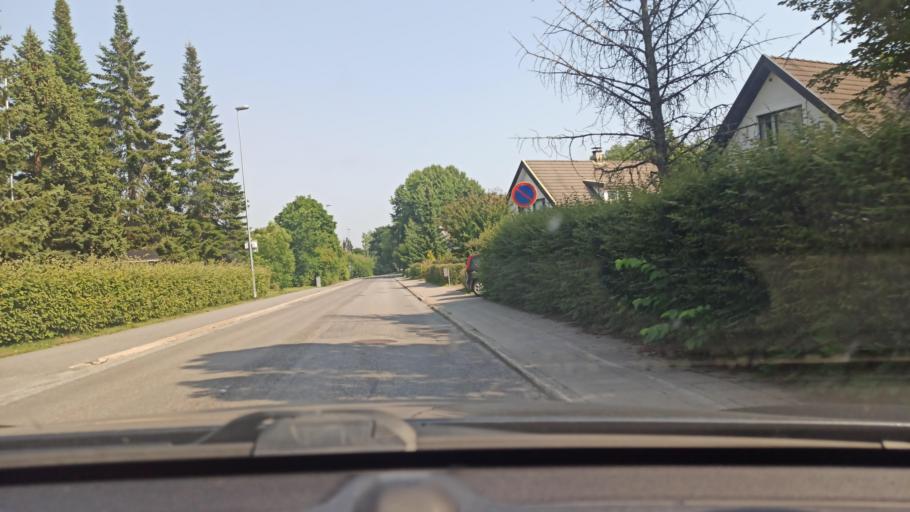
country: FI
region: Varsinais-Suomi
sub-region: Turku
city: Turku
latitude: 60.4608
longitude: 22.2290
